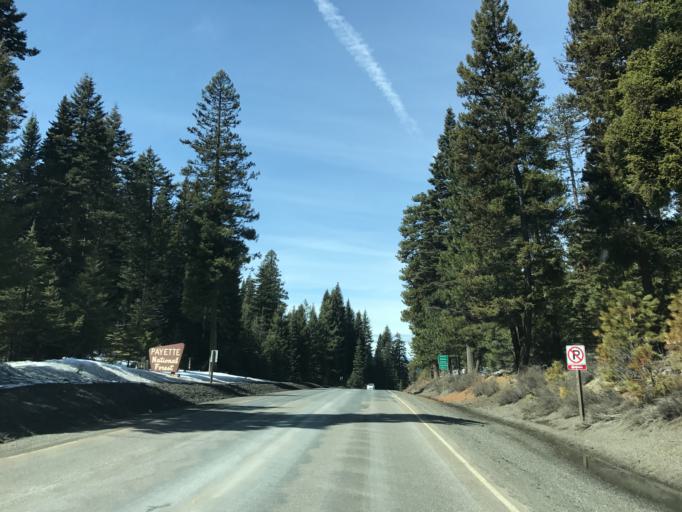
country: US
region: Idaho
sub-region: Valley County
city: McCall
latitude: 44.9296
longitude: -116.1555
